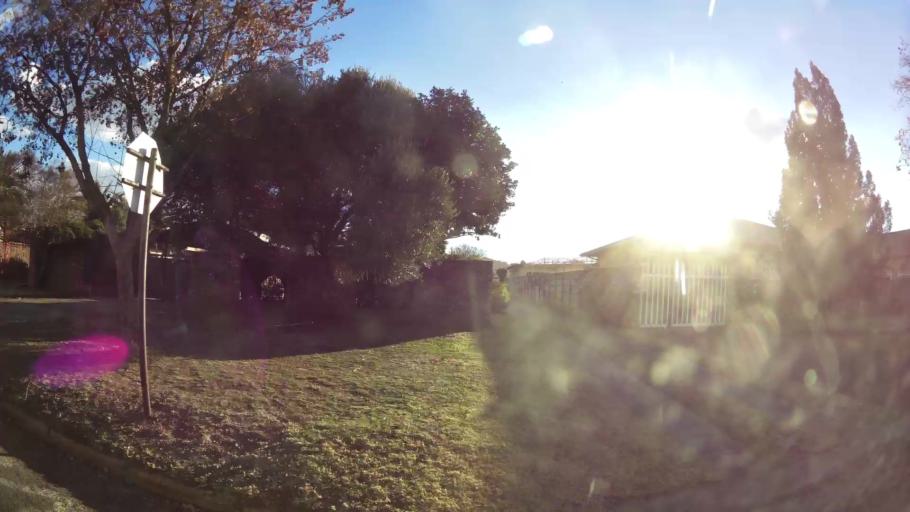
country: ZA
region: North-West
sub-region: Dr Kenneth Kaunda District Municipality
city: Potchefstroom
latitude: -26.7305
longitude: 27.0895
